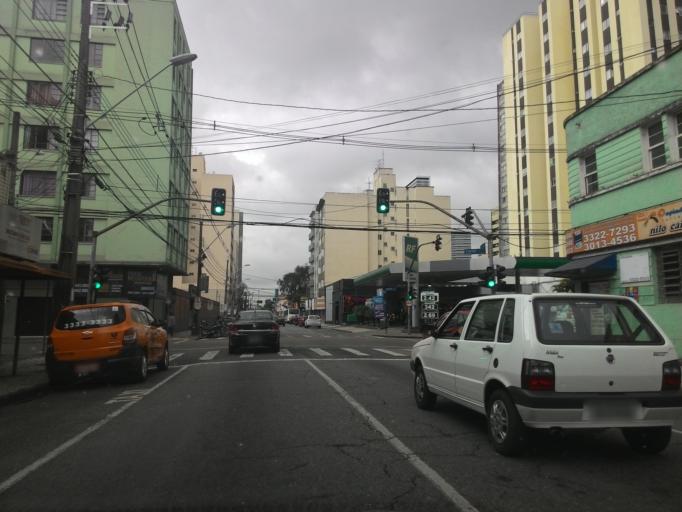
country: BR
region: Parana
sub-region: Curitiba
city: Curitiba
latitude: -25.4321
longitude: -49.2628
